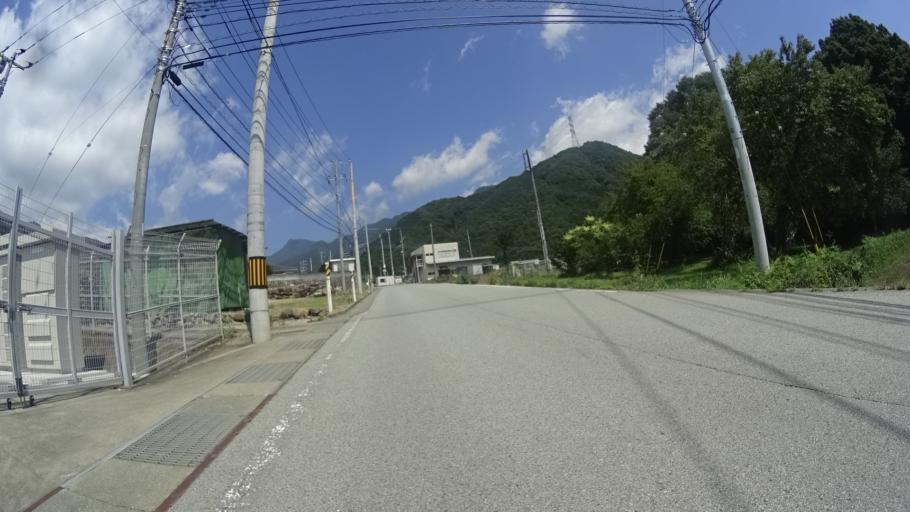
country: JP
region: Yamanashi
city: Enzan
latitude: 35.7673
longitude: 138.7039
